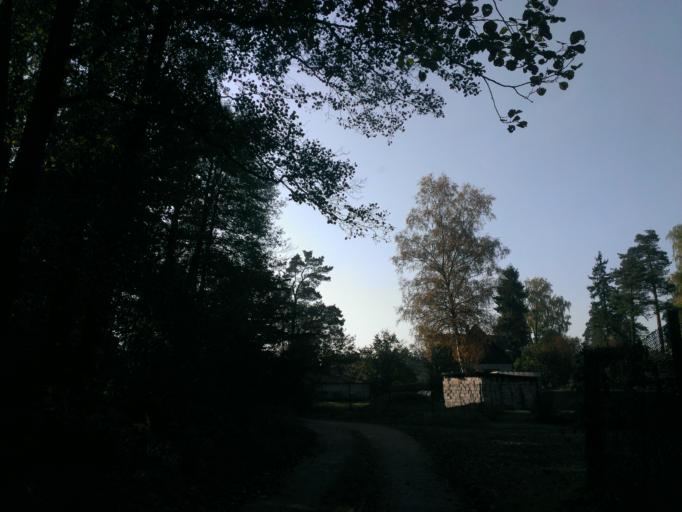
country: LV
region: Garkalne
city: Garkalne
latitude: 57.0447
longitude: 24.4237
